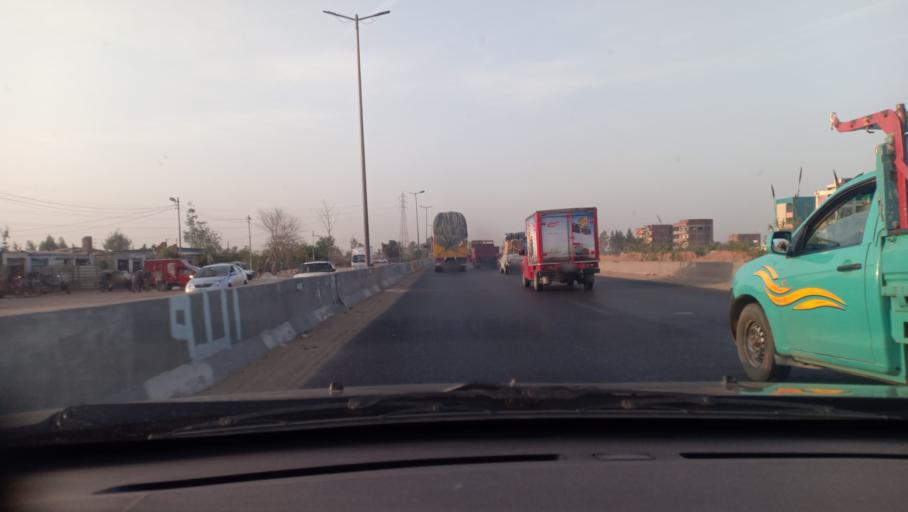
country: EG
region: Muhafazat al Minufiyah
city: Quwaysina
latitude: 30.5633
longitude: 31.2699
